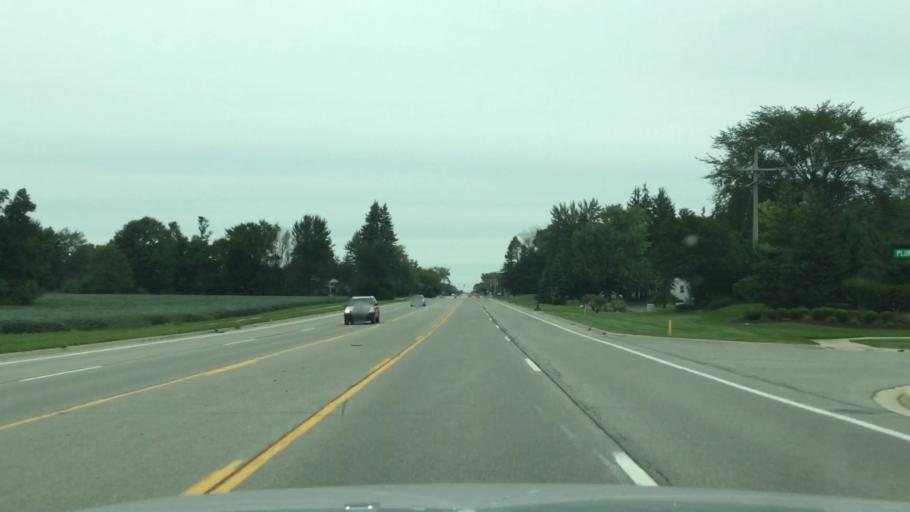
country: US
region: Michigan
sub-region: Washtenaw County
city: Ypsilanti
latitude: 42.2036
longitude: -83.6794
